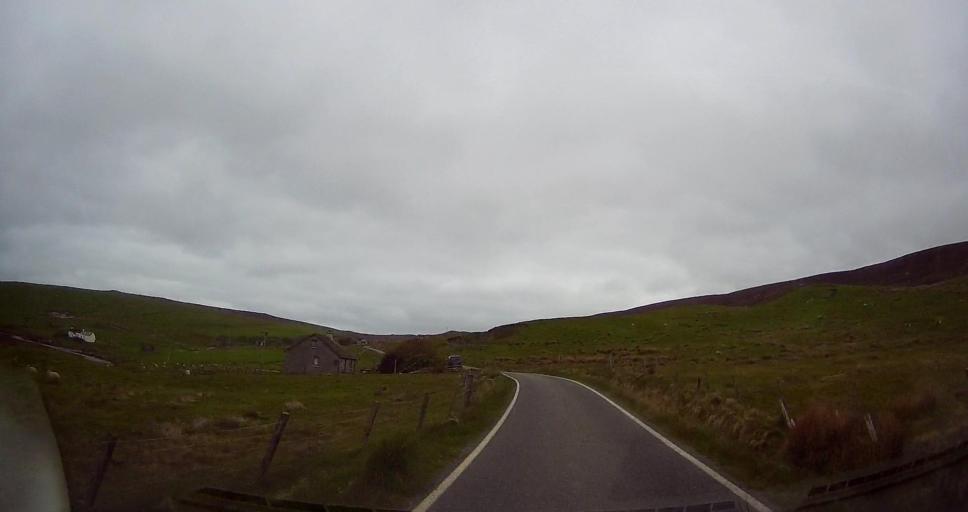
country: GB
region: Scotland
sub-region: Shetland Islands
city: Lerwick
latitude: 60.3012
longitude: -1.3371
